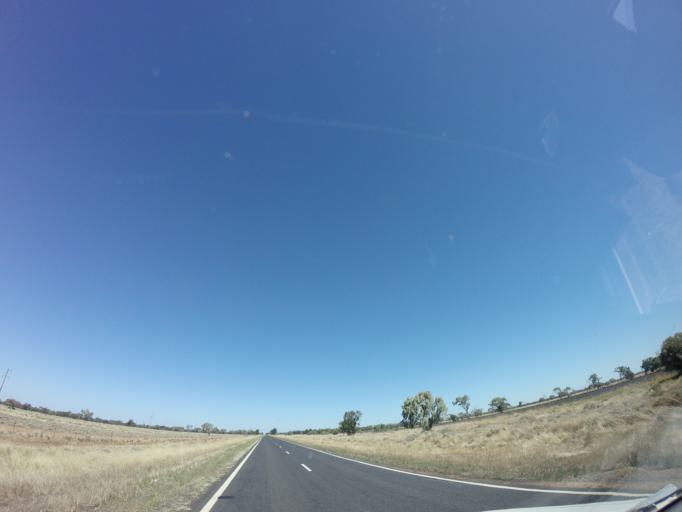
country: AU
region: New South Wales
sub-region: Bogan
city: Nyngan
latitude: -31.6282
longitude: 147.3213
